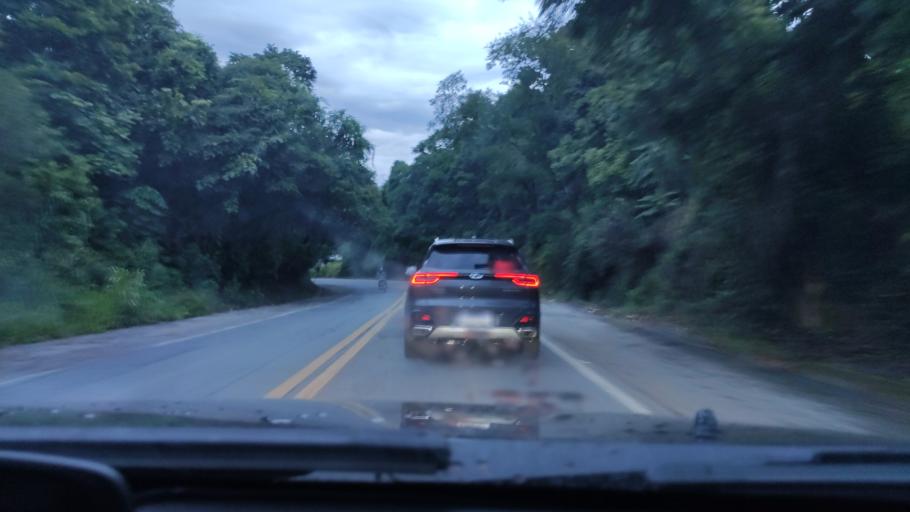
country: BR
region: Sao Paulo
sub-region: Socorro
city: Socorro
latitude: -22.5999
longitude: -46.5200
